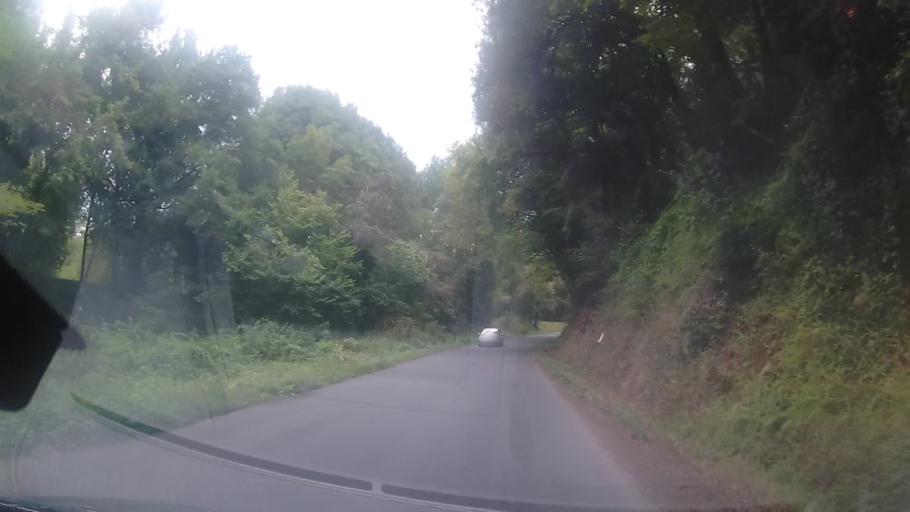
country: FR
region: Aquitaine
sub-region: Departement de la Dordogne
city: Carsac-Aillac
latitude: 44.8438
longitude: 1.3070
